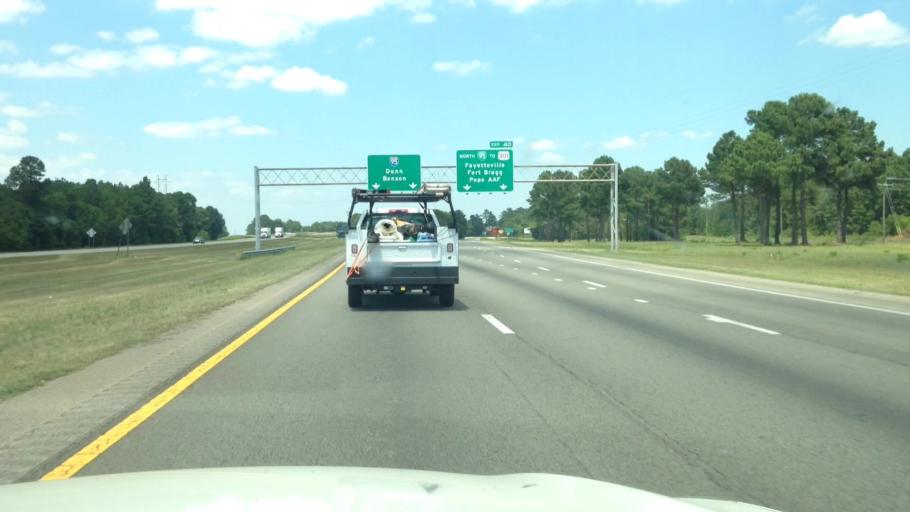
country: US
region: North Carolina
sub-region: Cumberland County
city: Hope Mills
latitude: 34.9232
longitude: -78.9447
